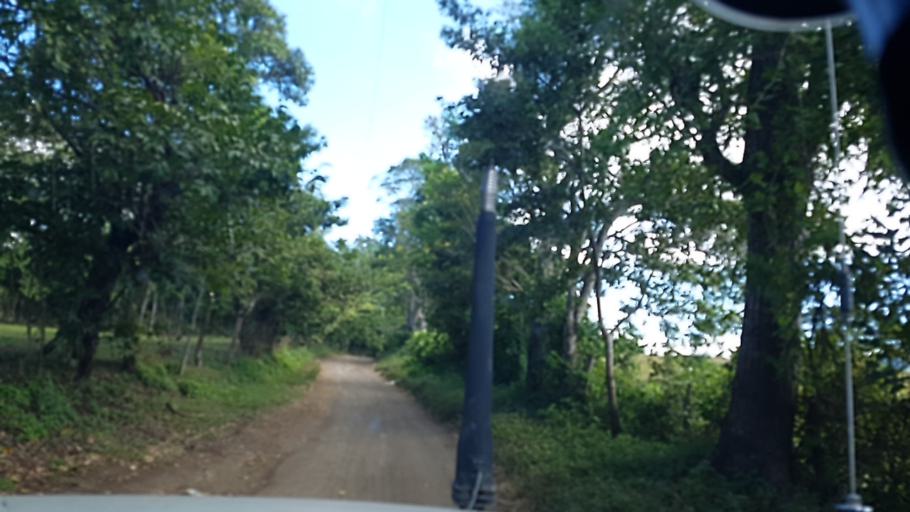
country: NI
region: Carazo
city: La Paz de Oriente
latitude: 11.8244
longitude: -86.1380
